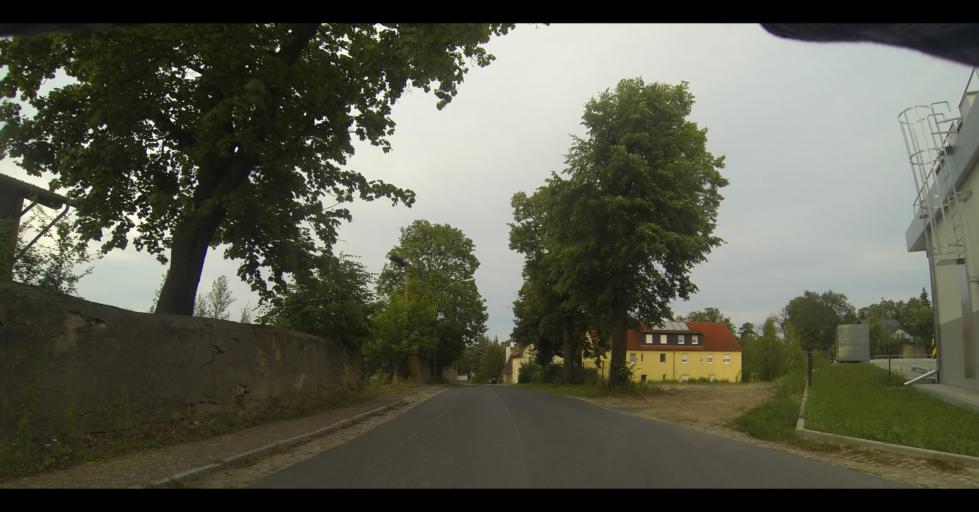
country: DE
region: Saxony
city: Radeburg
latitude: 51.2156
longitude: 13.7312
